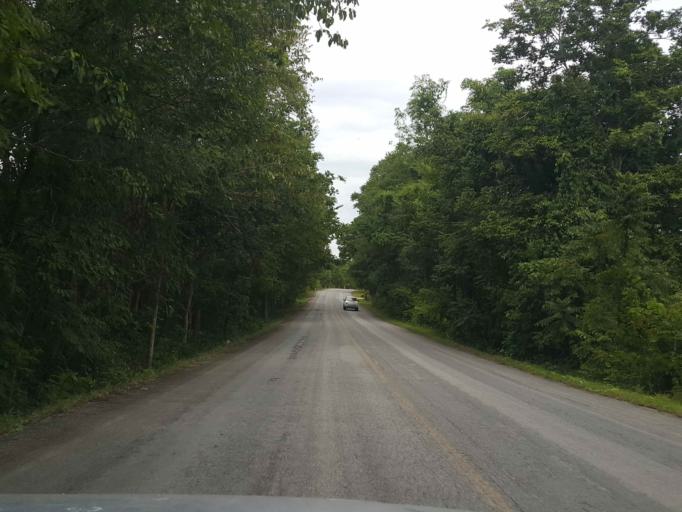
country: TH
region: Lampang
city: Thoen
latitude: 17.6311
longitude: 99.2709
